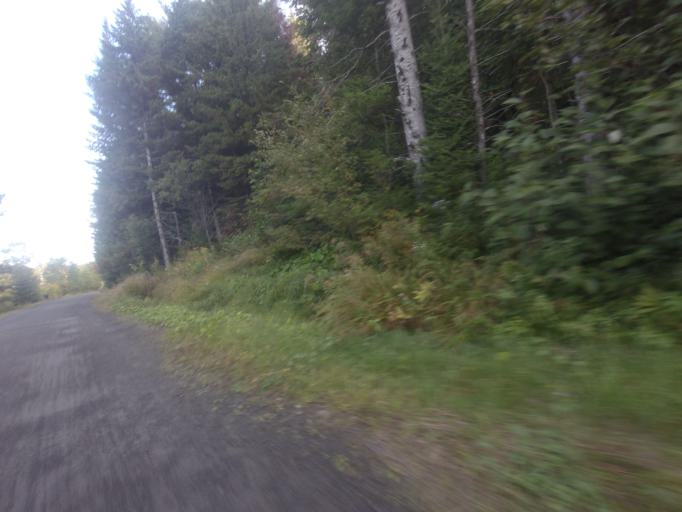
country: CA
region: Quebec
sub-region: Laurentides
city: Sainte-Adele
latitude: 45.9496
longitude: -74.1130
